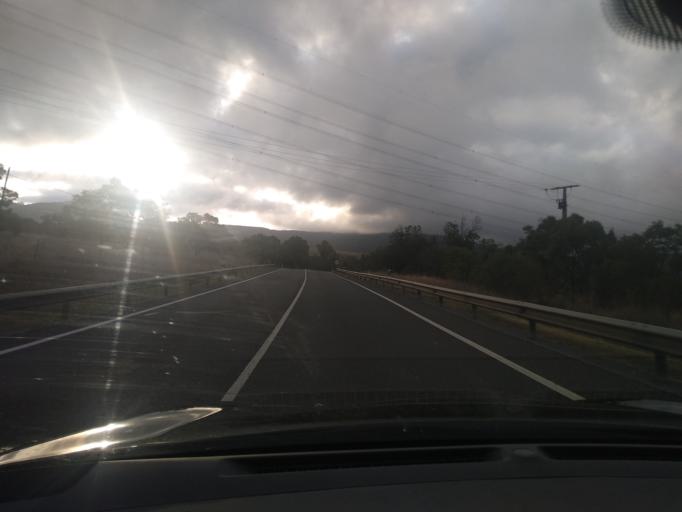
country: ES
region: Castille and Leon
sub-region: Provincia de Segovia
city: Otero de Herreros
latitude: 40.7539
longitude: -4.2053
